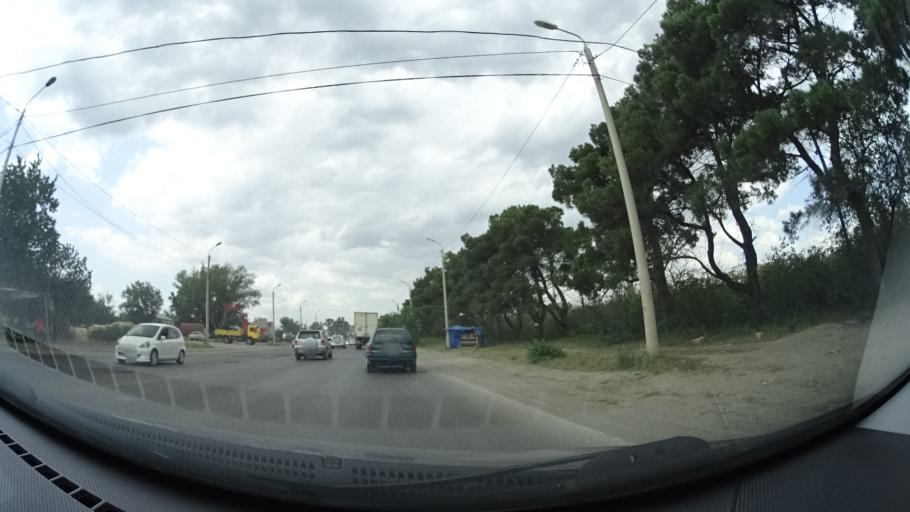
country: GE
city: Didi Lilo
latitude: 41.6927
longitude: 44.9715
